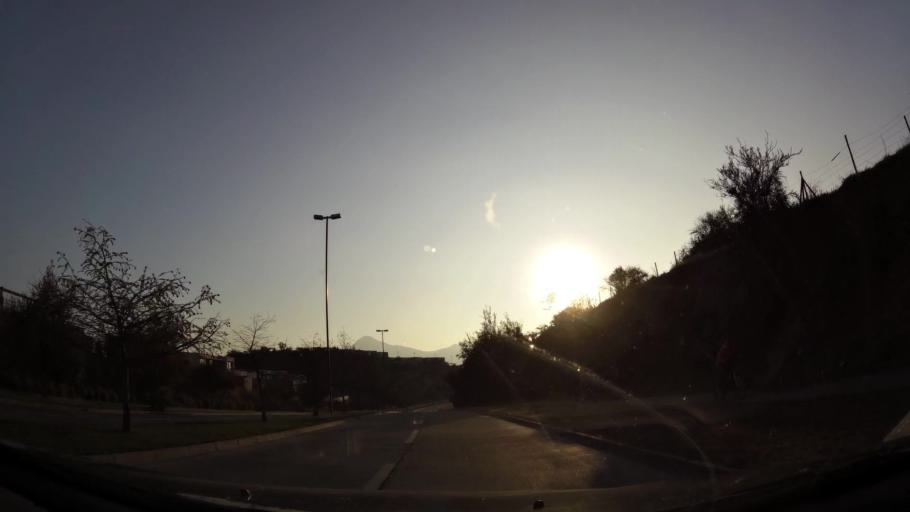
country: CL
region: Santiago Metropolitan
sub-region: Provincia de Santiago
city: Villa Presidente Frei, Nunoa, Santiago, Chile
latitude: -33.3330
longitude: -70.5073
